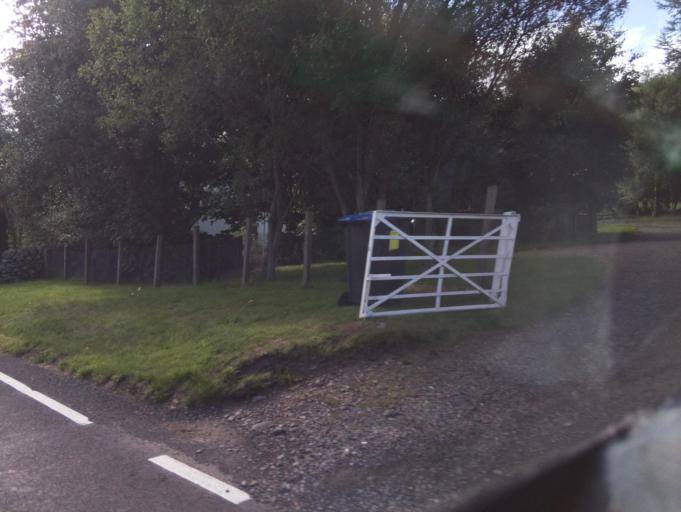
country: GB
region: Scotland
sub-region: South Lanarkshire
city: Biggar
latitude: 55.5164
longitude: -3.4164
